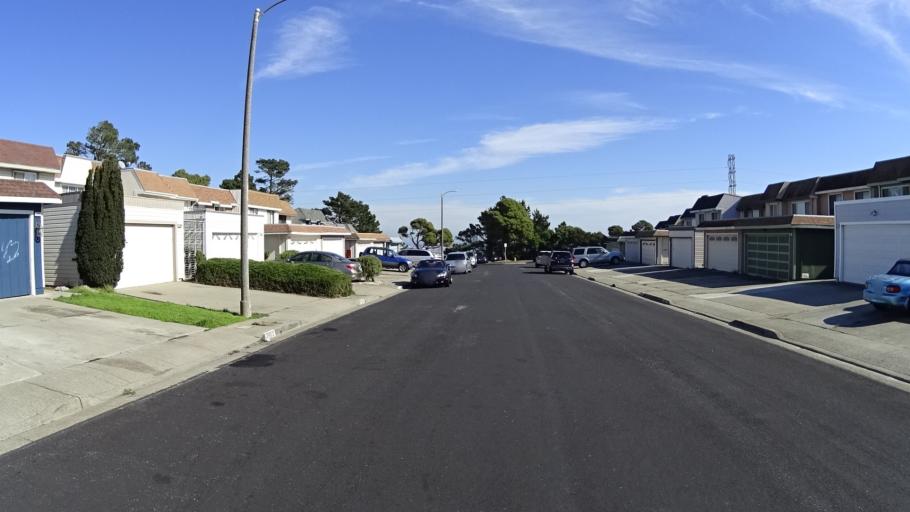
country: US
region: California
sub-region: San Mateo County
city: Colma
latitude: 37.6475
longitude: -122.4559
